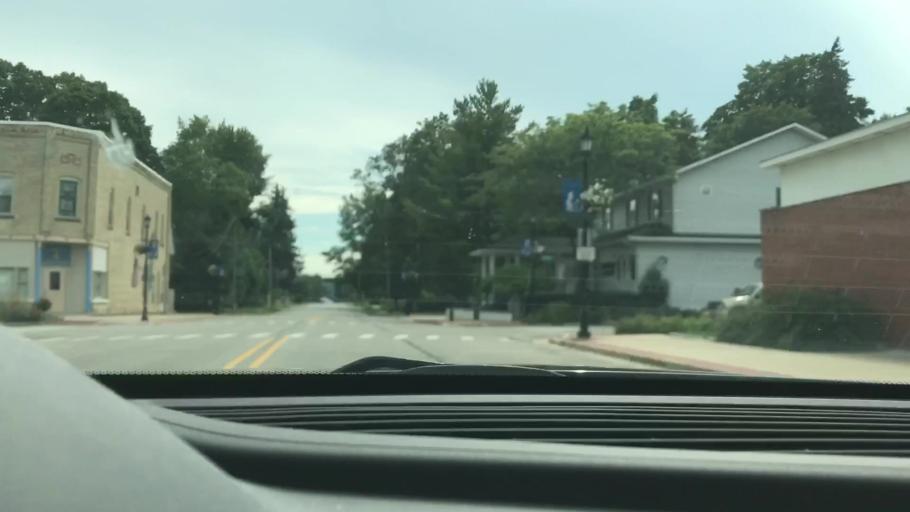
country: US
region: Michigan
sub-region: Antrim County
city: Bellaire
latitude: 45.0697
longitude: -85.2642
